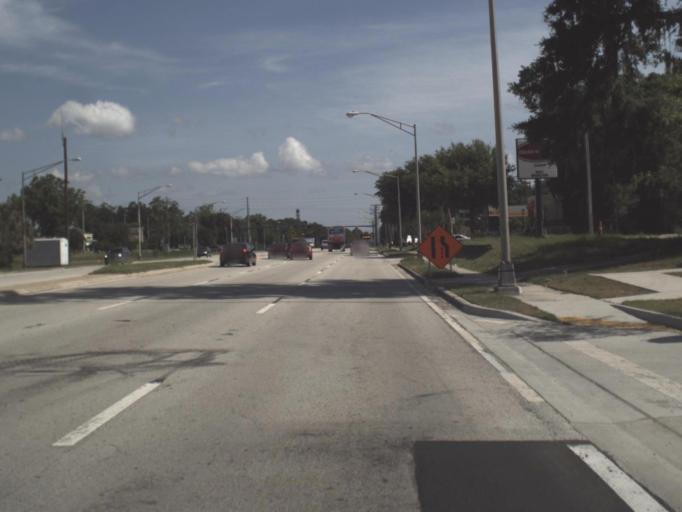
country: US
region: Florida
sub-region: Duval County
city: Jacksonville
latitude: 30.2860
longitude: -81.7201
